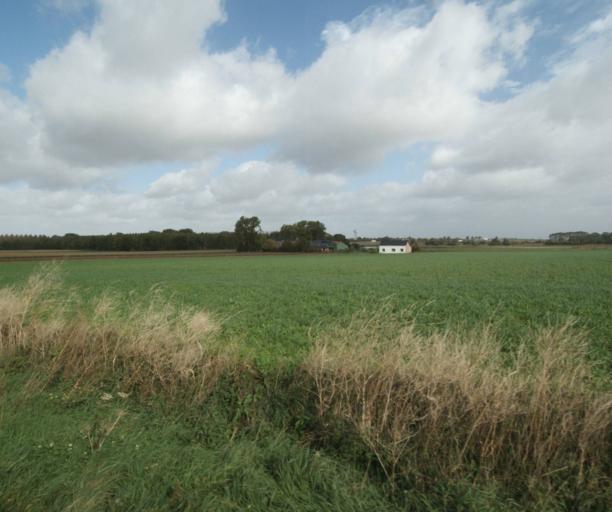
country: FR
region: Nord-Pas-de-Calais
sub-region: Departement du Nord
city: Fournes-en-Weppes
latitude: 50.5719
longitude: 2.8866
